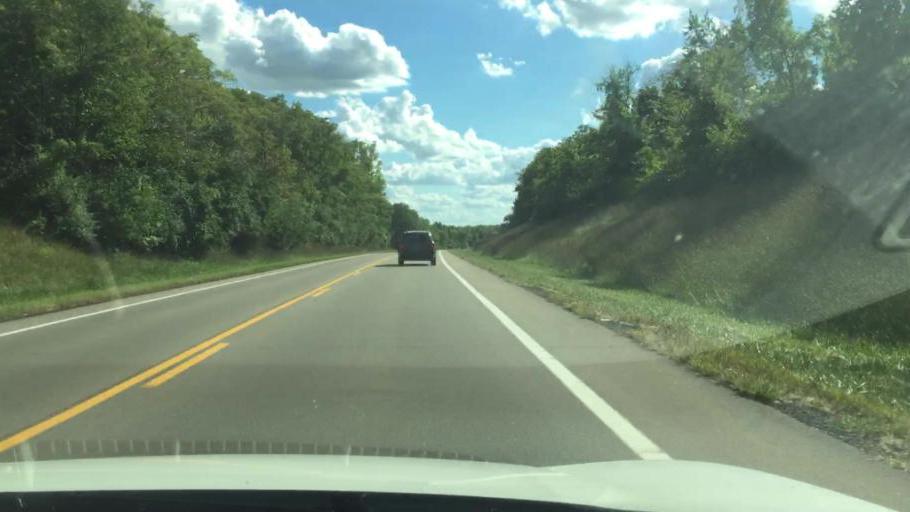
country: US
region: Ohio
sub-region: Clark County
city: Northridge
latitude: 39.9906
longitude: -83.7308
